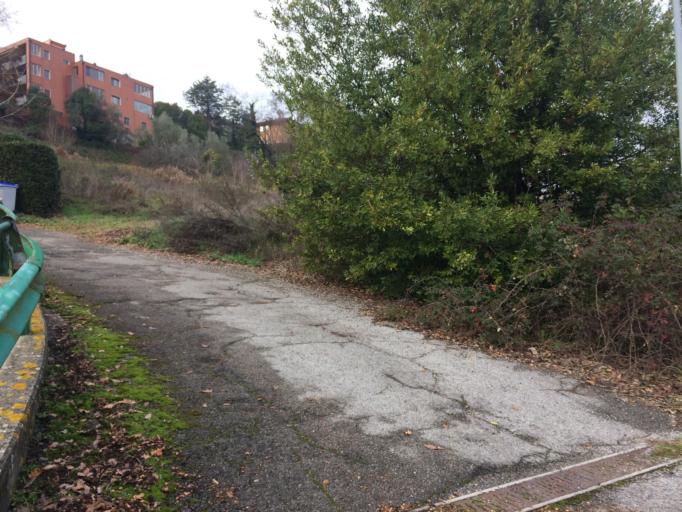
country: IT
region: Umbria
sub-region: Provincia di Perugia
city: Perugia
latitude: 43.0979
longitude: 12.4015
